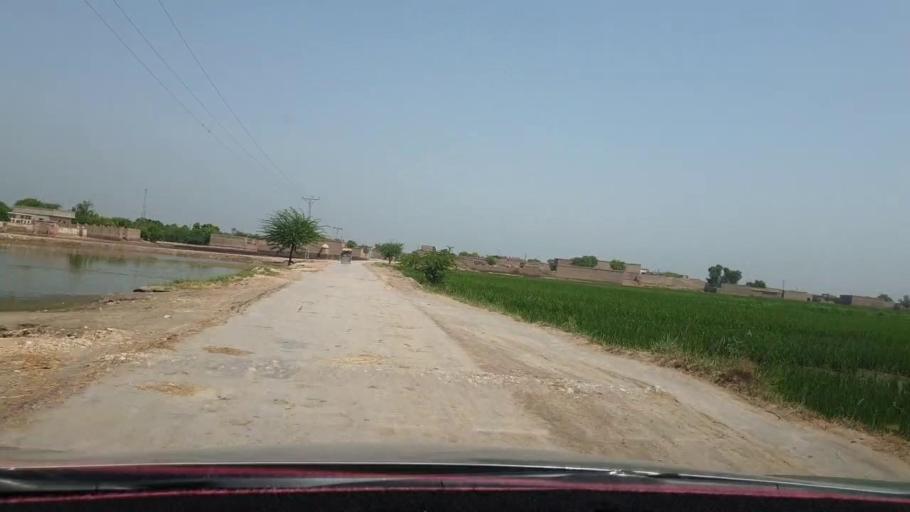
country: PK
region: Sindh
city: Warah
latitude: 27.4418
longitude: 67.7764
